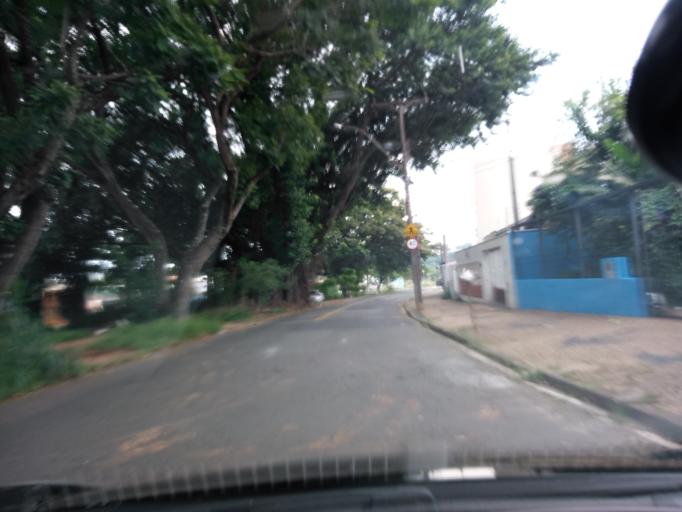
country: BR
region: Sao Paulo
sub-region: Campinas
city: Campinas
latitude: -22.8778
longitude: -47.0370
